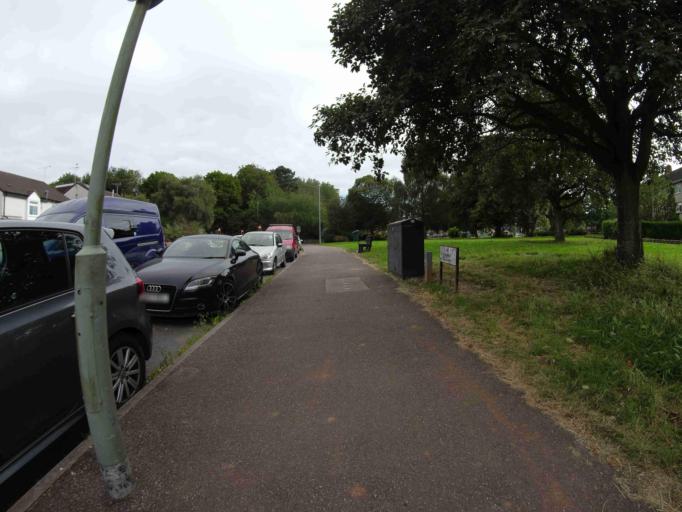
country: GB
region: England
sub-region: Devon
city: Heavitree
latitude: 50.7206
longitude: -3.4920
